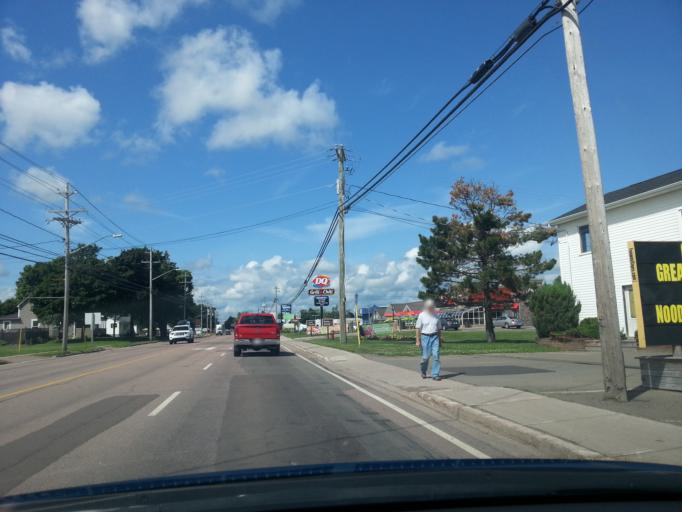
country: CA
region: New Brunswick
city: Shediac
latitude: 46.2253
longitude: -64.5091
